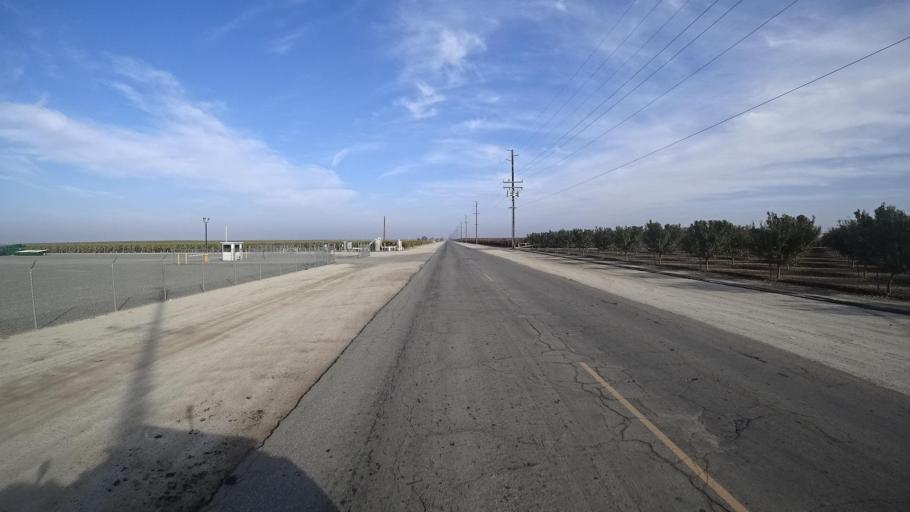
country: US
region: California
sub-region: Kern County
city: McFarland
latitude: 35.7064
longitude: -119.2050
